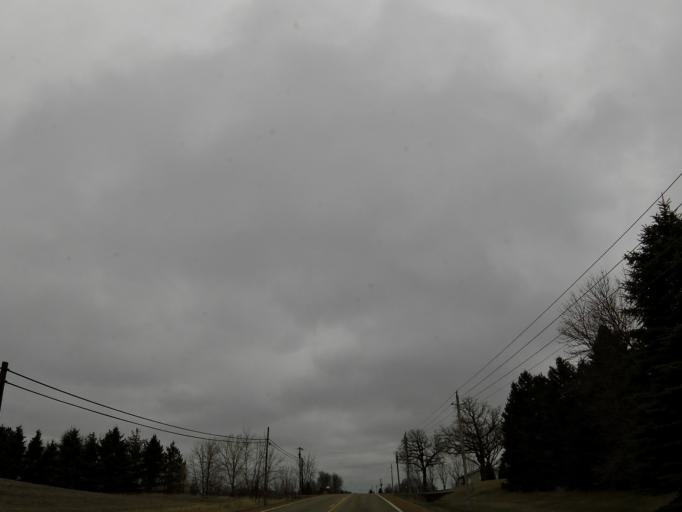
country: US
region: Minnesota
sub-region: Scott County
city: Shakopee
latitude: 44.7568
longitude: -93.5411
